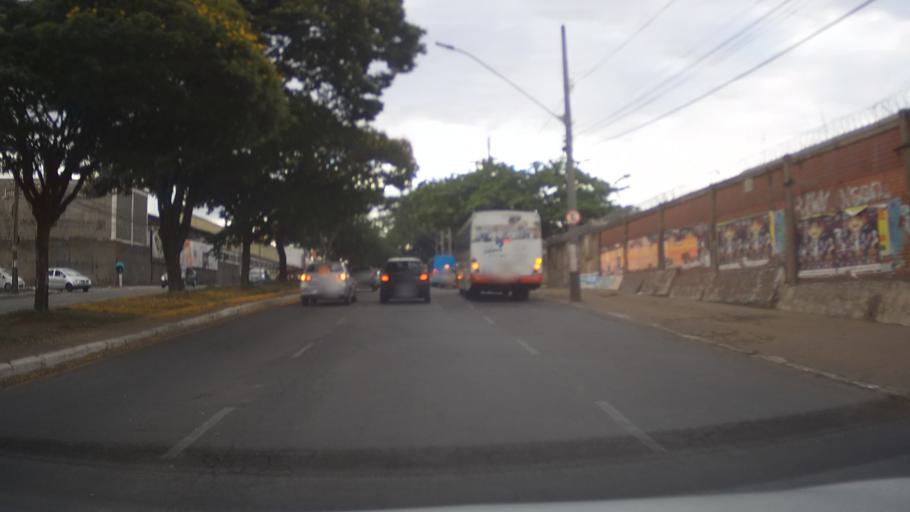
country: BR
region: Minas Gerais
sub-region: Contagem
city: Contagem
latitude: -19.9549
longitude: -44.0173
